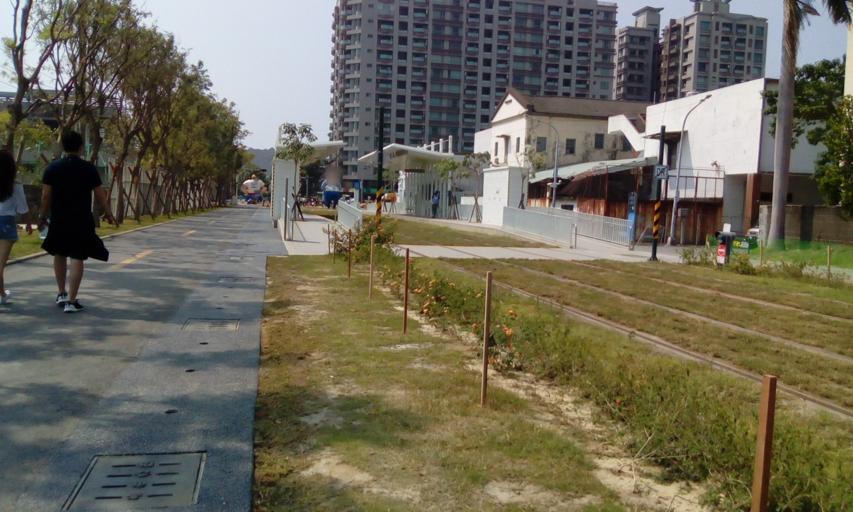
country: TW
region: Kaohsiung
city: Kaohsiung
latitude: 22.6202
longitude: 120.2803
